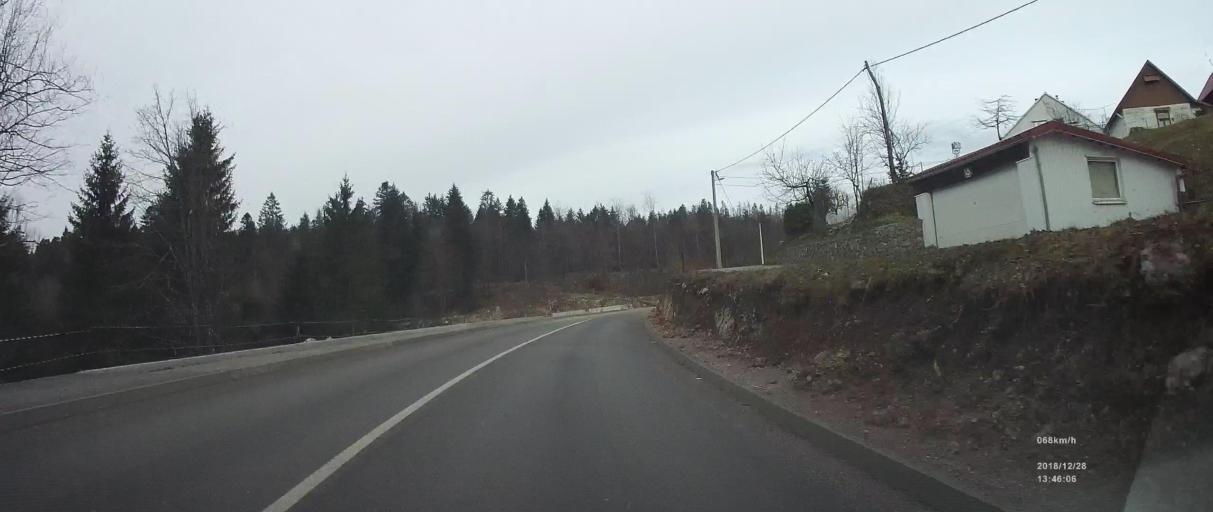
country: HR
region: Primorsko-Goranska
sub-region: Grad Delnice
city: Delnice
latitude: 45.3850
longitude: 14.7897
